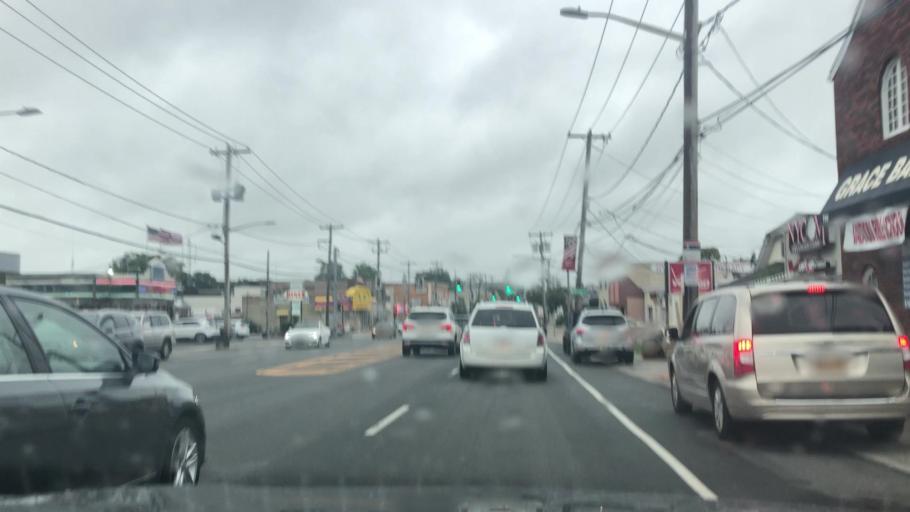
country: US
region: New York
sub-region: Nassau County
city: Franklin Square
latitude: 40.7069
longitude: -73.6692
